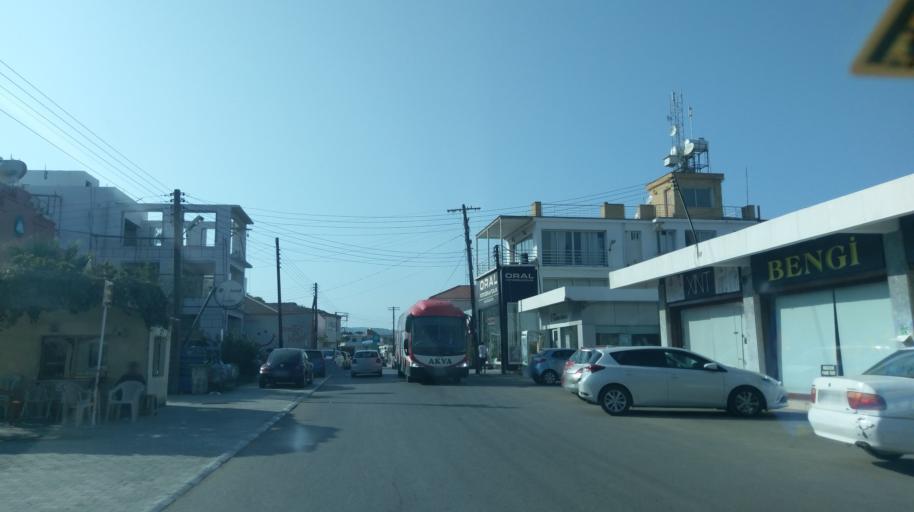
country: CY
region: Lefkosia
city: Lefka
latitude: 35.1415
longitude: 32.8337
